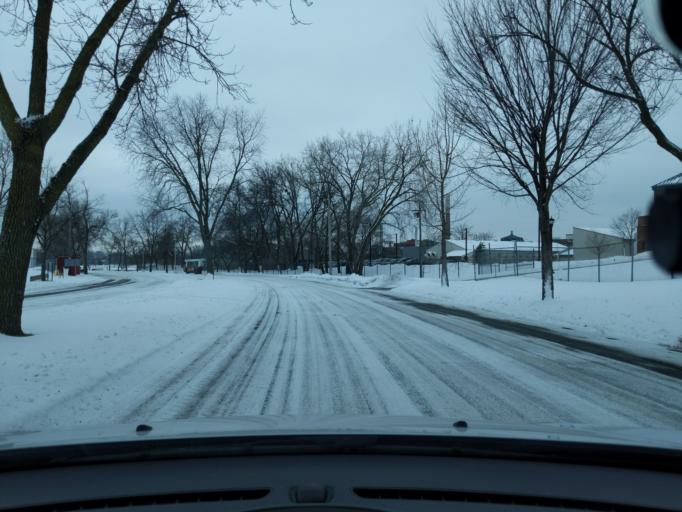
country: US
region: Minnesota
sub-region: Ramsey County
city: Falcon Heights
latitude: 44.9831
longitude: -93.1792
